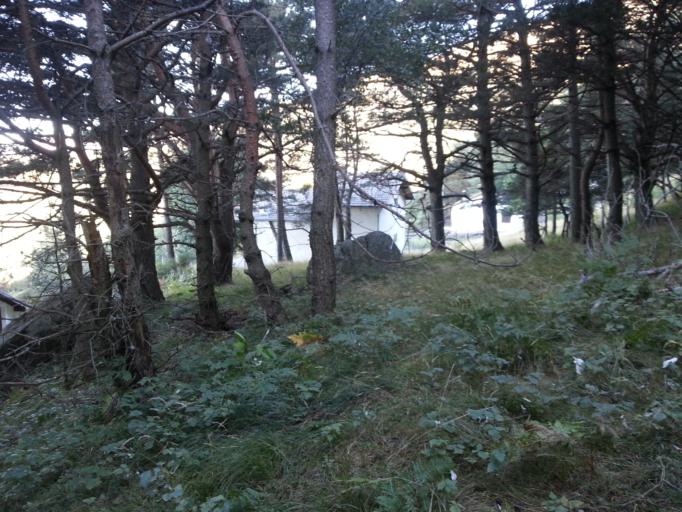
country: IT
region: Lombardy
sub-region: Provincia di Como
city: Montemezzo
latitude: 46.1943
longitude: 9.3852
